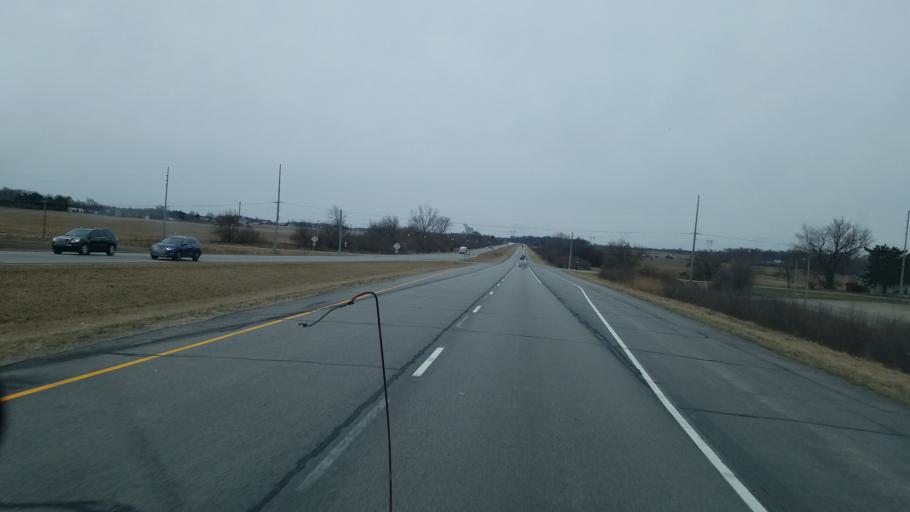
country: US
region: Indiana
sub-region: Marshall County
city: Argos
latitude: 41.2323
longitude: -86.2618
